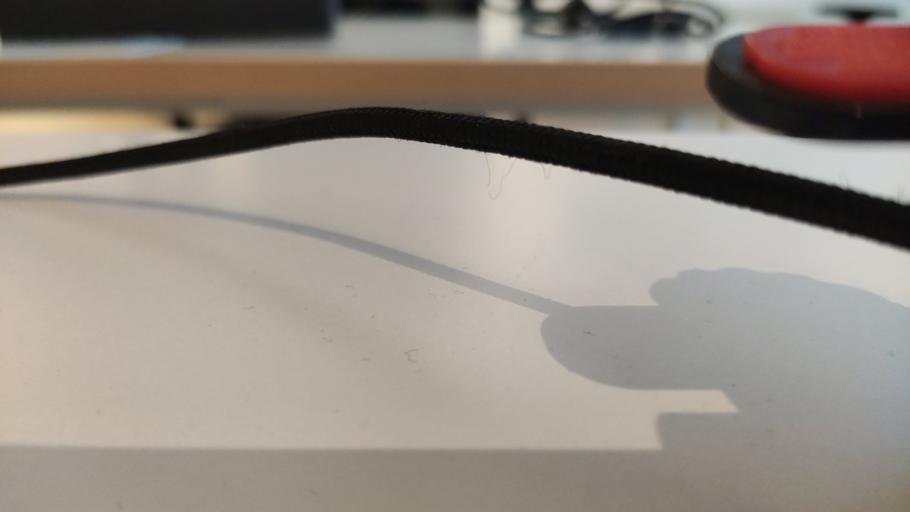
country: RU
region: Moskovskaya
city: Novopetrovskoye
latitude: 55.8801
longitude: 36.4133
